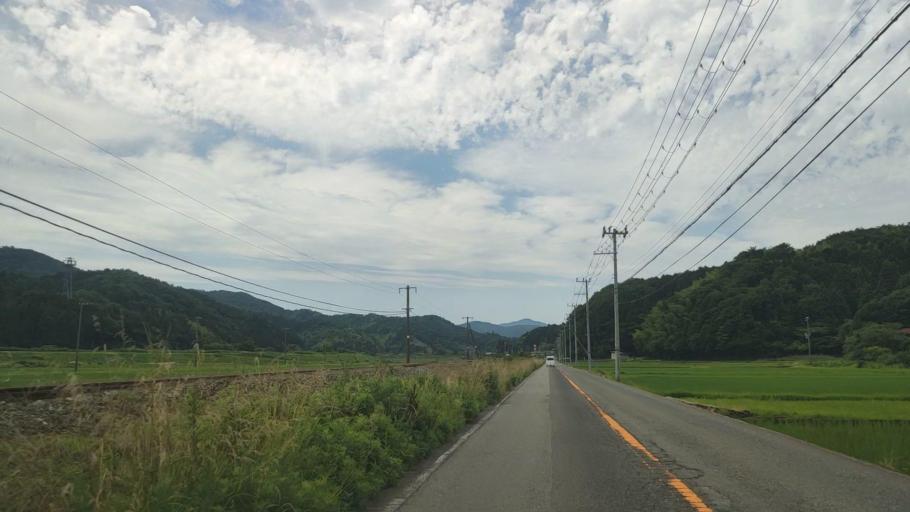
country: JP
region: Hyogo
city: Toyooka
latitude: 35.6395
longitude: 134.7577
